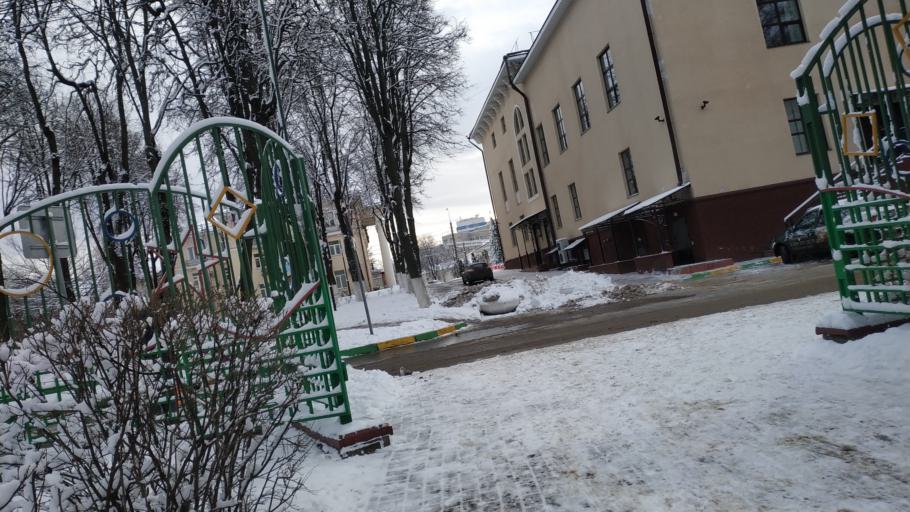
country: RU
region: Moskovskaya
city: Vidnoye
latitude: 55.5580
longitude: 37.7084
